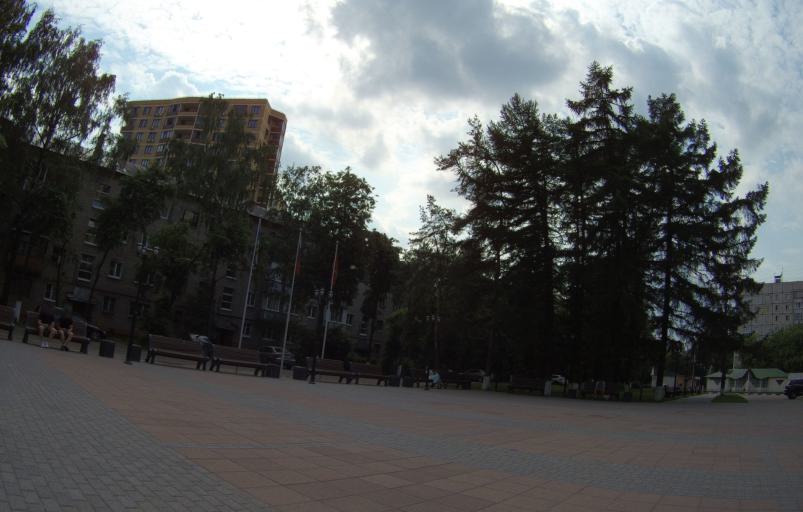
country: RU
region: Moskovskaya
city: Vereya
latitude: 55.6296
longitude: 38.0541
